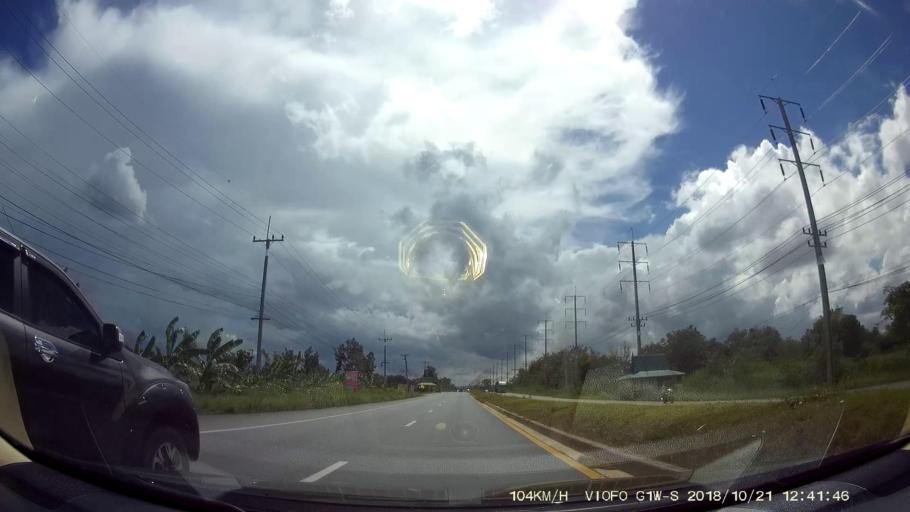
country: TH
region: Nakhon Ratchasima
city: Amphoe Sikhiu
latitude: 15.0081
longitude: 101.6863
